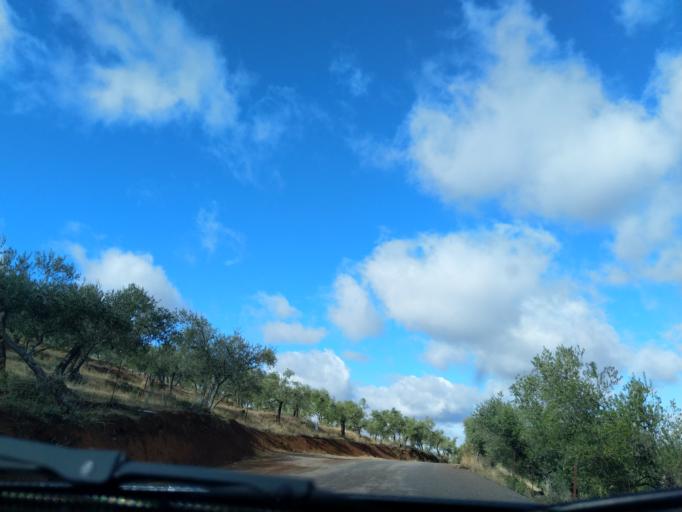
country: ES
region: Extremadura
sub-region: Provincia de Badajoz
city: Reina
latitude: 38.1275
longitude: -5.9223
